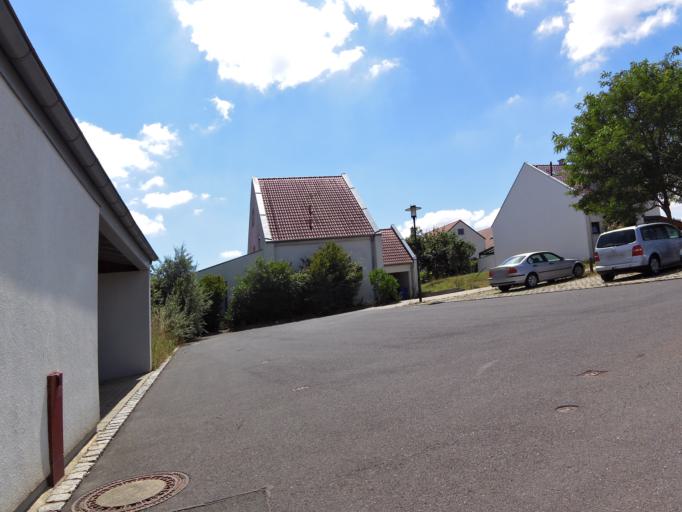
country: DE
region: Bavaria
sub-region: Regierungsbezirk Unterfranken
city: Gerbrunn
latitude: 49.7847
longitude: 9.9930
